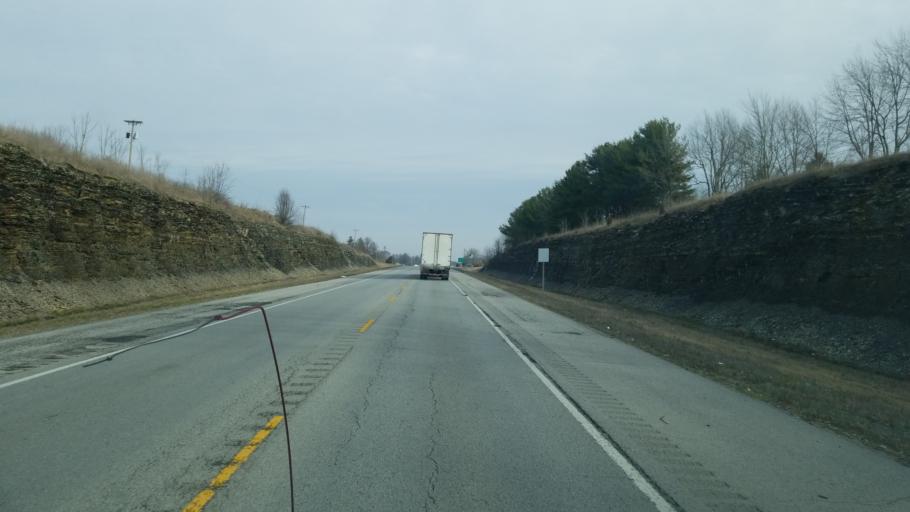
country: US
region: Kentucky
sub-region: Boyle County
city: Junction City
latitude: 37.5720
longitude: -84.7942
